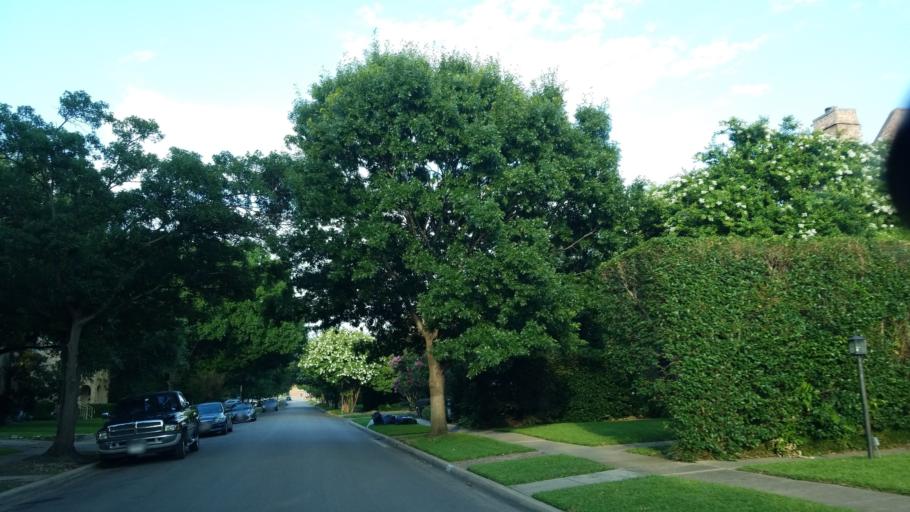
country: US
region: Texas
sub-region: Dallas County
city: Highland Park
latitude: 32.8429
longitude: -96.7912
